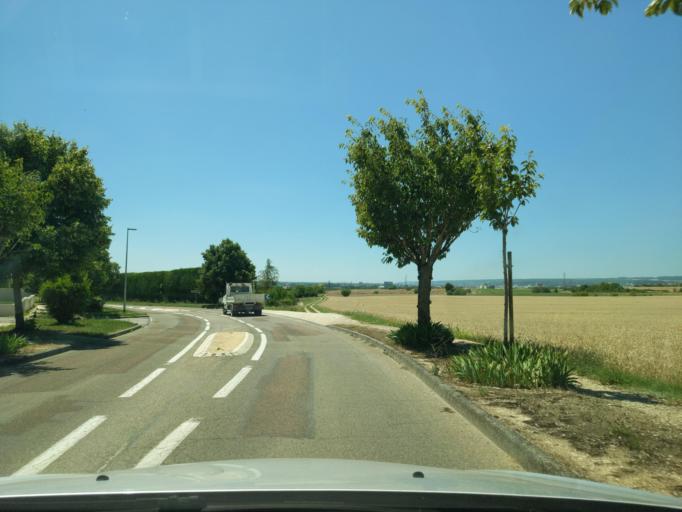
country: FR
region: Bourgogne
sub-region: Departement de la Cote-d'Or
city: Ruffey-les-Echirey
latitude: 47.3767
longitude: 5.0688
